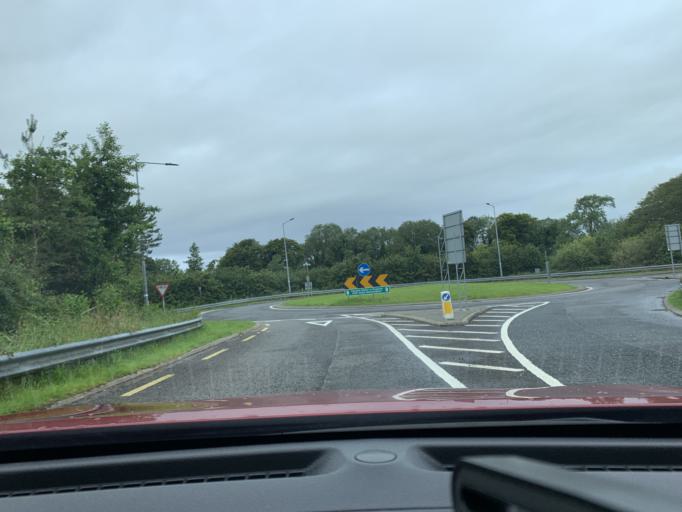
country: IE
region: Ulster
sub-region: County Donegal
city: Ballyshannon
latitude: 54.4976
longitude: -8.1854
